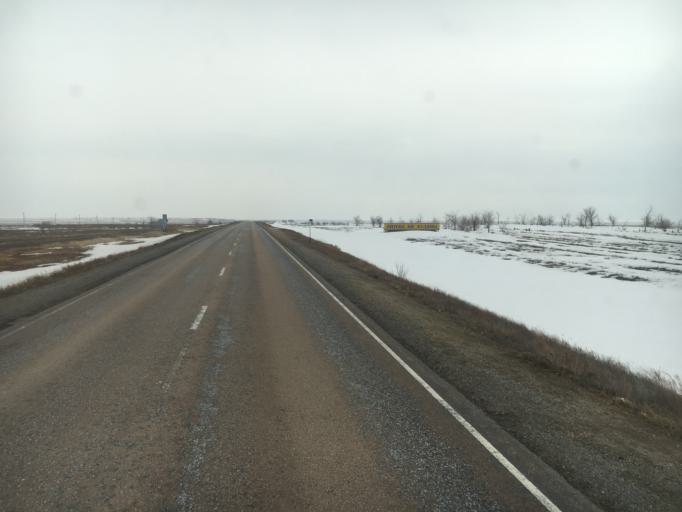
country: RU
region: Orenburg
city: Dombarovskiy
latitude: 50.0937
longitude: 59.4892
